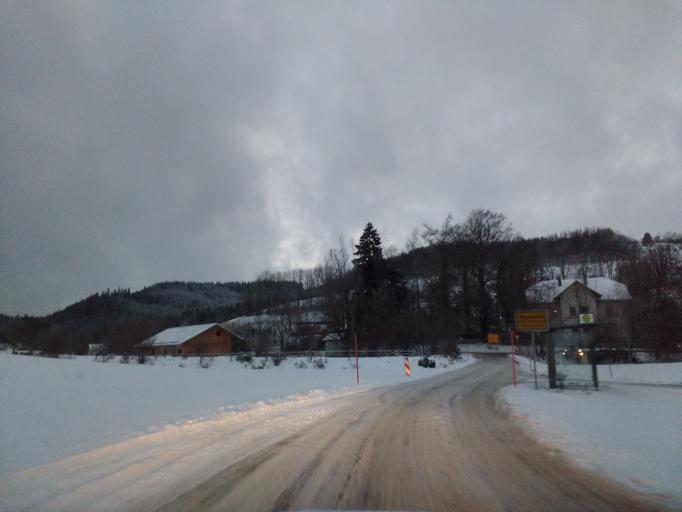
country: DE
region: Bavaria
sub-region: Swabia
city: Buchenberg
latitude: 47.7186
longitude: 10.2171
